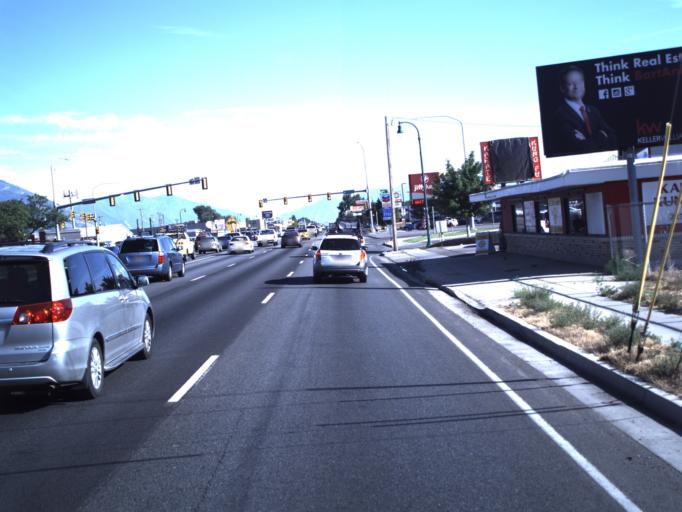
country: US
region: Utah
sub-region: Utah County
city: Orem
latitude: 40.3130
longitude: -111.7021
